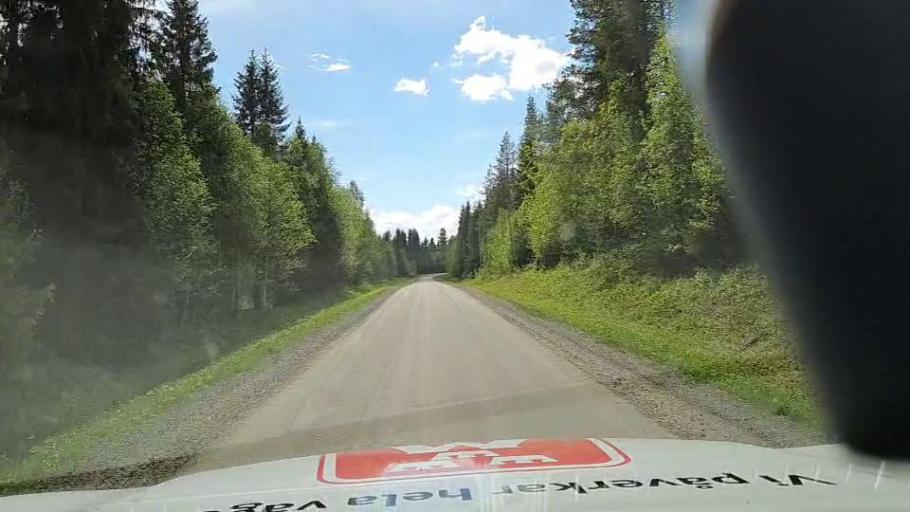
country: SE
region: Vaesterbotten
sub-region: Vilhelmina Kommun
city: Sjoberg
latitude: 64.5480
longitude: 15.7935
